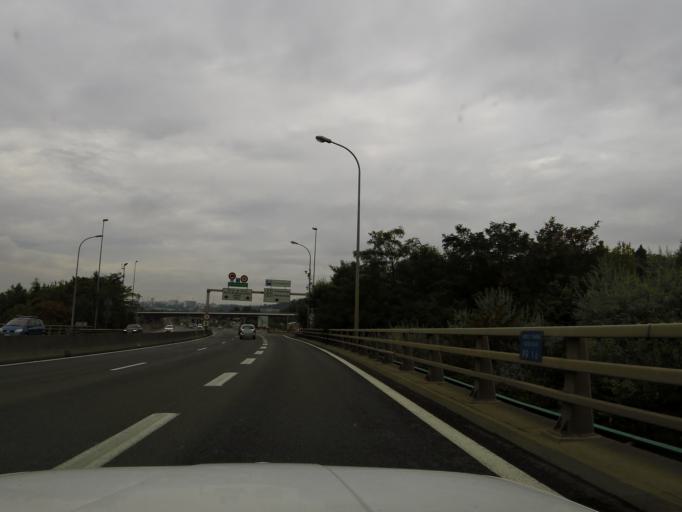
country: FR
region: Rhone-Alpes
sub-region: Departement du Rhone
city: Villeurbanne
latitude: 45.7937
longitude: 4.8761
